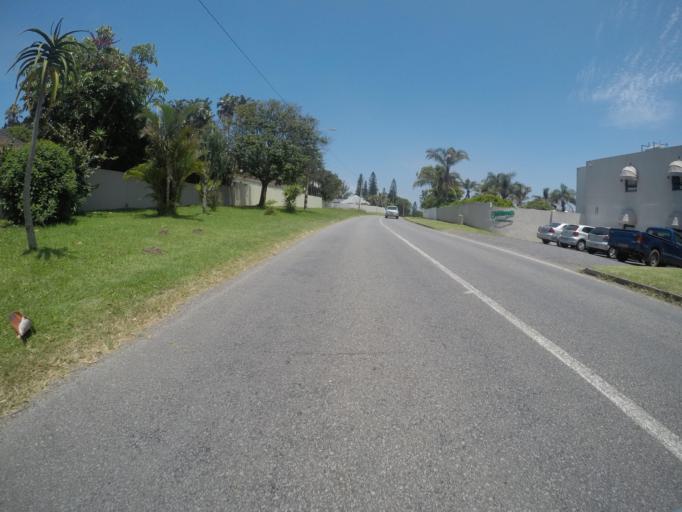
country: ZA
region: Eastern Cape
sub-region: Buffalo City Metropolitan Municipality
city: East London
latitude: -32.9967
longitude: 27.9255
